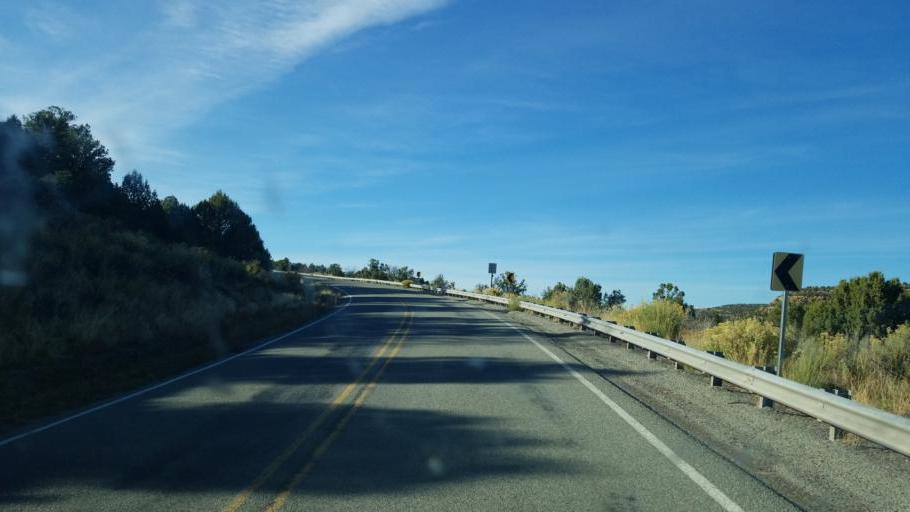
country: US
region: New Mexico
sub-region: Rio Arriba County
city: Navajo
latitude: 36.7099
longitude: -107.3192
